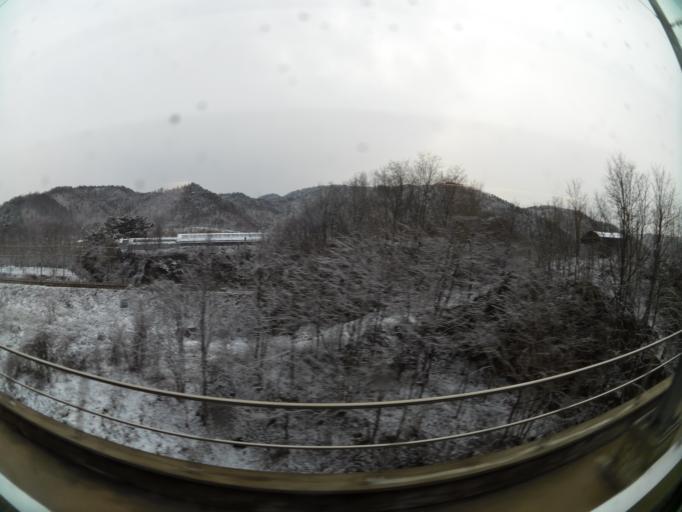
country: KR
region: Chungcheongbuk-do
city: Yong-dong
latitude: 36.1975
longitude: 127.7542
